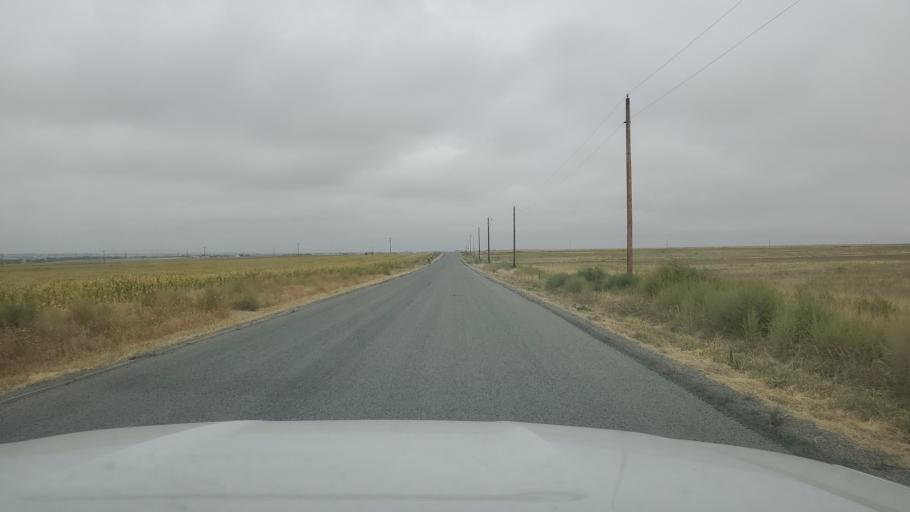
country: US
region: Colorado
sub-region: Weld County
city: Lochbuie
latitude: 39.9239
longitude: -104.6027
